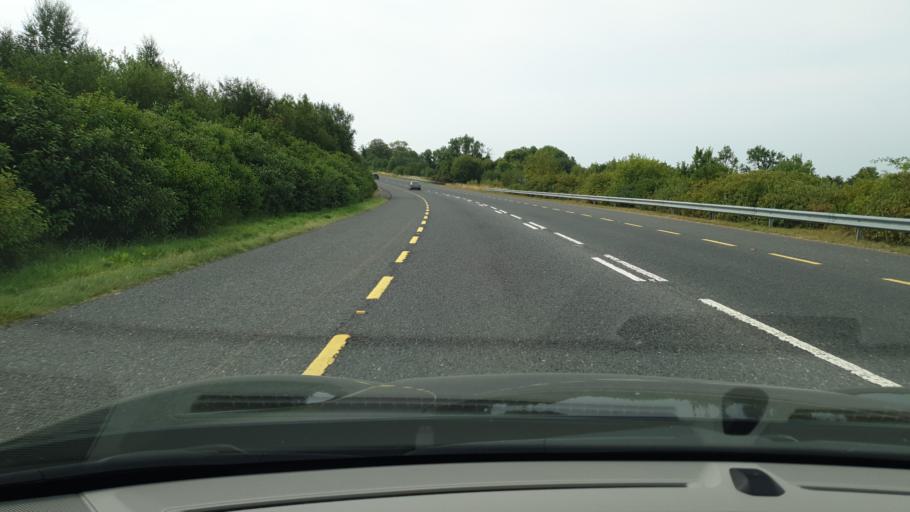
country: IE
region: Leinster
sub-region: An Mhi
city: Navan
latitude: 53.6378
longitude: -6.7429
